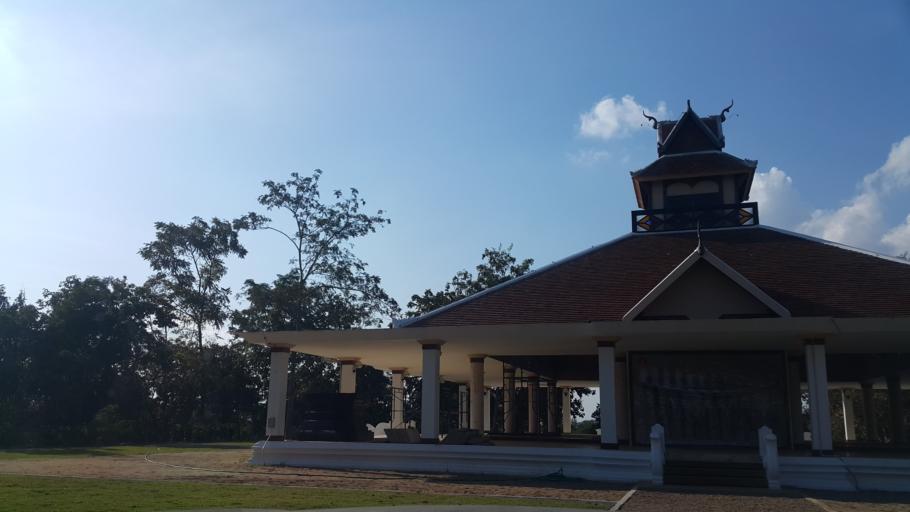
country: TH
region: Lamphun
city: Mae Tha
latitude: 18.5106
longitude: 99.1128
